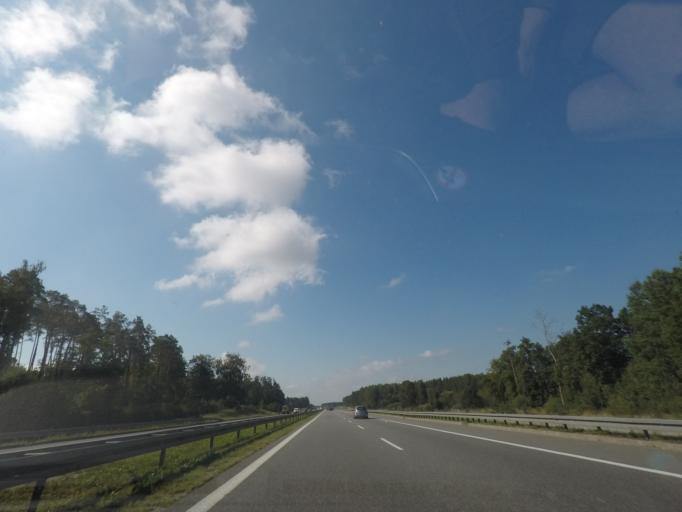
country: PL
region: Pomeranian Voivodeship
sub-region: Powiat tczewski
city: Pelplin
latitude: 54.0180
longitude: 18.6649
